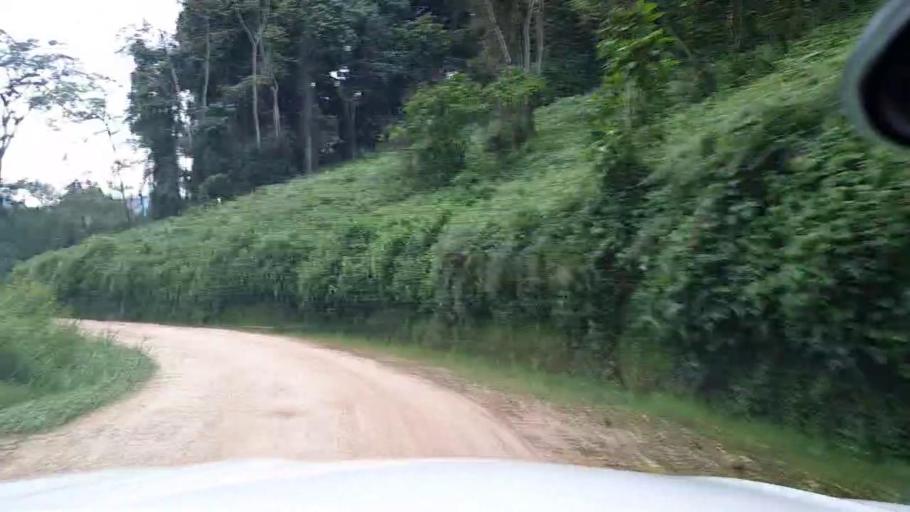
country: RW
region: Western Province
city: Cyangugu
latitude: -2.5584
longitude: 29.2300
